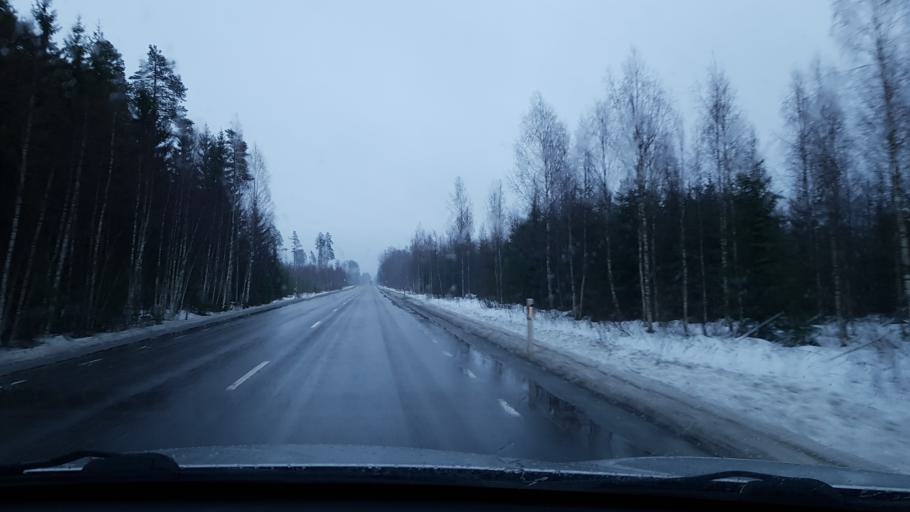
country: EE
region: Paernumaa
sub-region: Vaendra vald (alev)
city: Vandra
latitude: 58.8133
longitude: 25.1794
